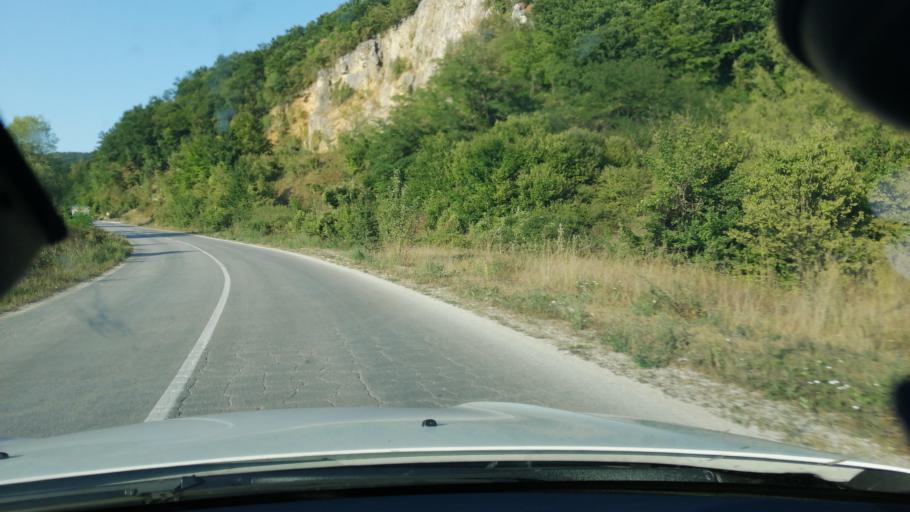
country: RS
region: Central Serbia
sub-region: Moravicki Okrug
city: Ivanjica
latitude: 43.7114
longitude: 20.2450
